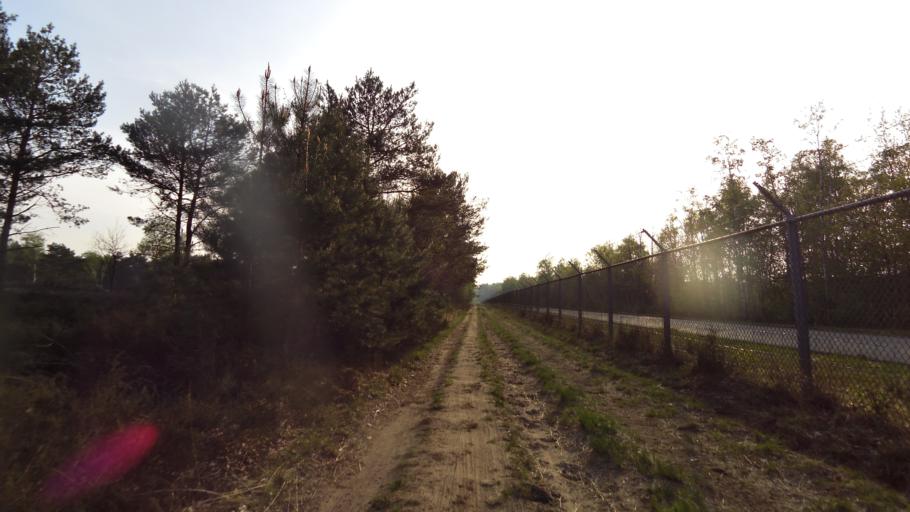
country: NL
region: Gelderland
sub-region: Gemeente Ede
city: Wekerom
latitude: 52.0657
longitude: 5.7028
